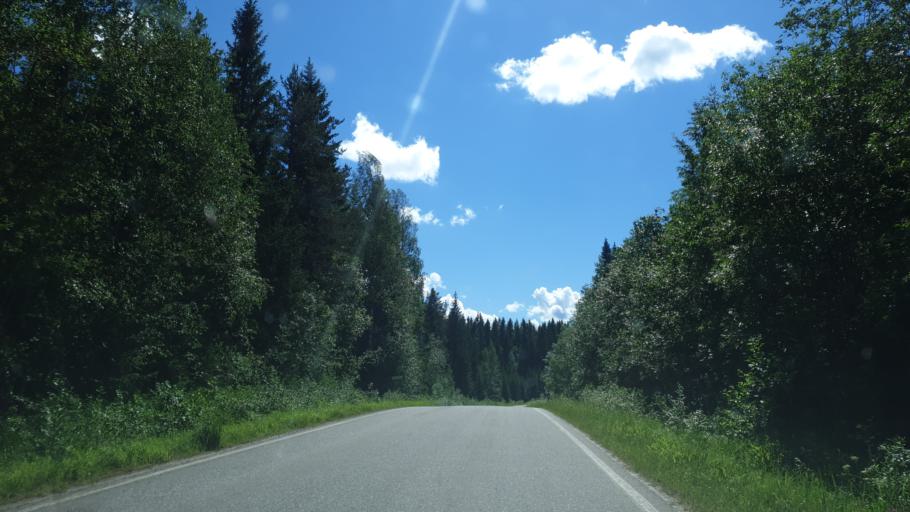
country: FI
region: Northern Savo
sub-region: Koillis-Savo
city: Kaavi
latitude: 63.0111
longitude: 28.5138
